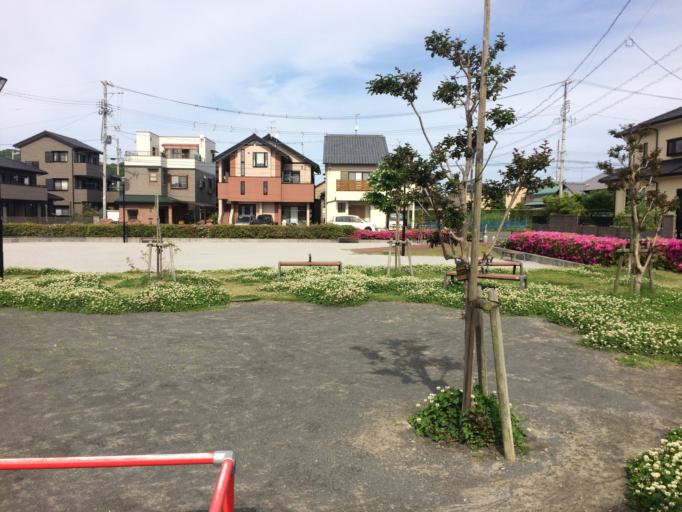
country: JP
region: Shizuoka
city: Shizuoka-shi
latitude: 34.9489
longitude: 138.4282
